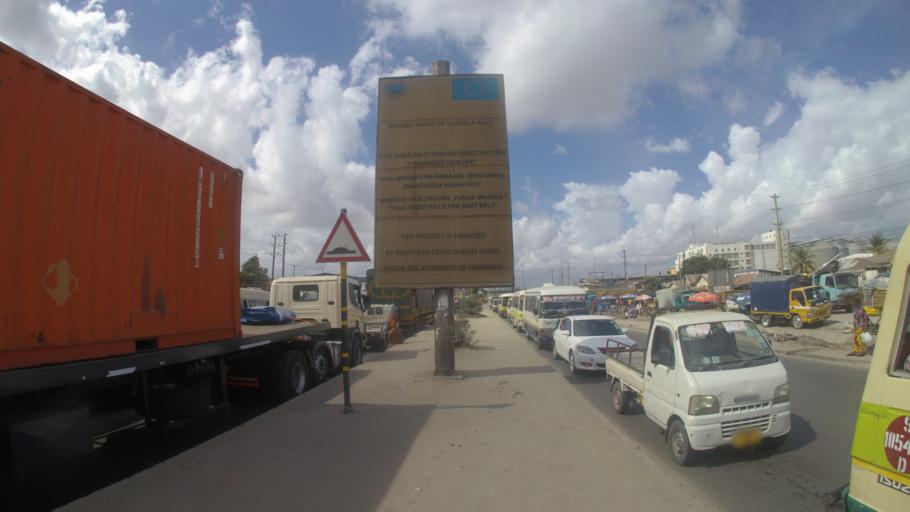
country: TZ
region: Dar es Salaam
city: Dar es Salaam
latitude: -6.8402
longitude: 39.2443
